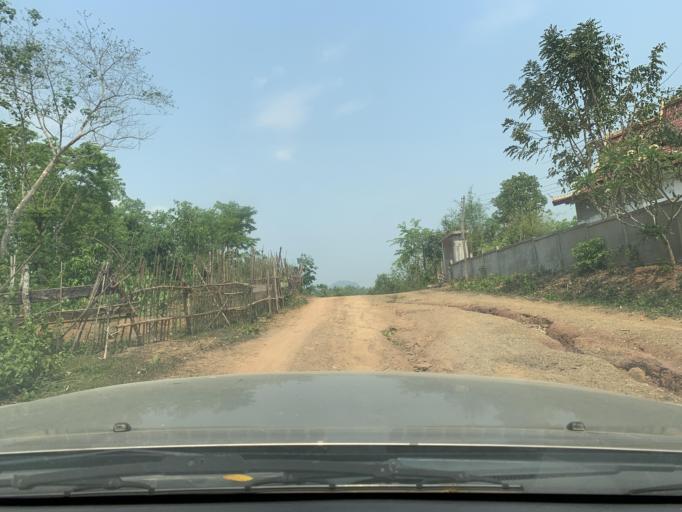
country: LA
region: Louangphabang
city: Louangphabang
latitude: 19.9368
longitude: 102.1486
